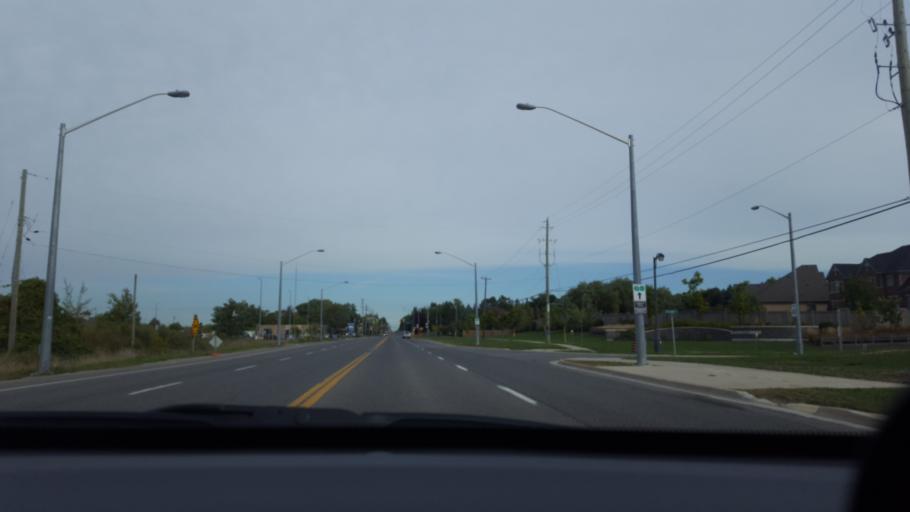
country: CA
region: Ontario
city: Vaughan
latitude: 43.9185
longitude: -79.5255
